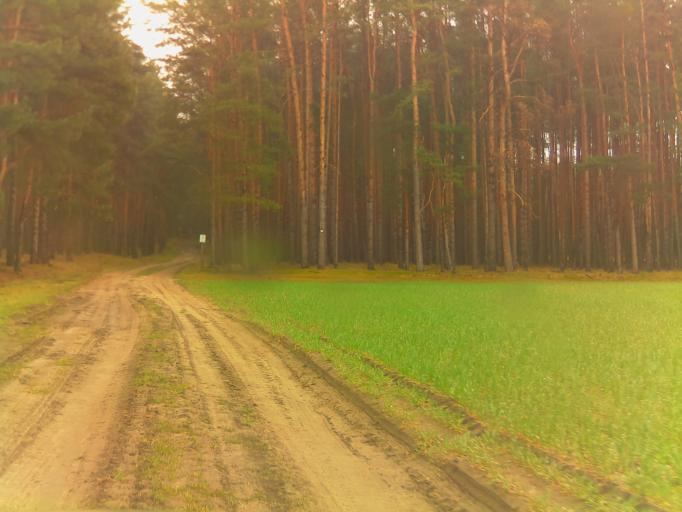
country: DE
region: Brandenburg
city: Friedland
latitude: 52.0338
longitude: 14.2330
